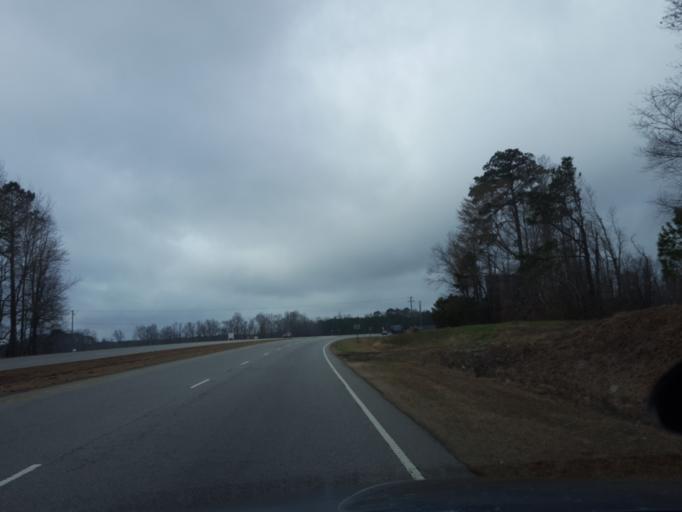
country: US
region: North Carolina
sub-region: Washington County
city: Plymouth
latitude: 35.8157
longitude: -76.8353
